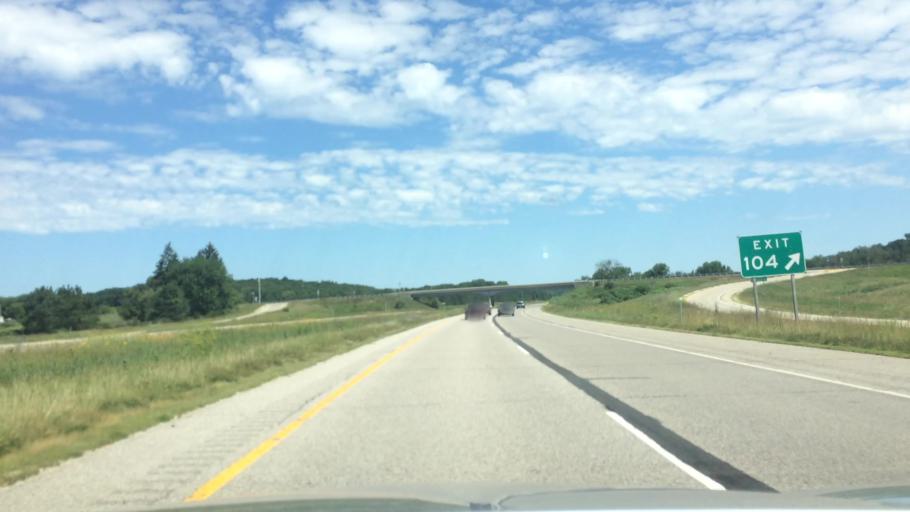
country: US
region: Wisconsin
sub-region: Marquette County
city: Westfield
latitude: 43.7568
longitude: -89.4836
